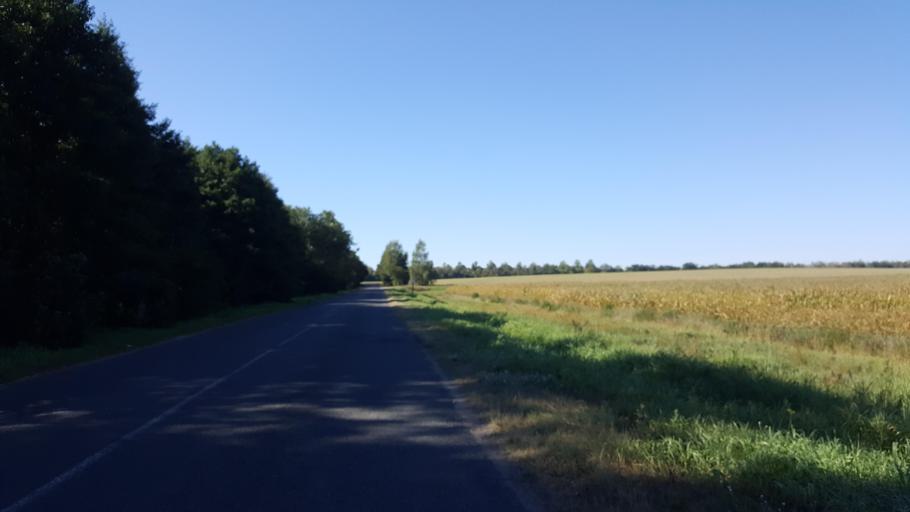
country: BY
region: Brest
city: Charnawchytsy
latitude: 52.3177
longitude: 23.6111
